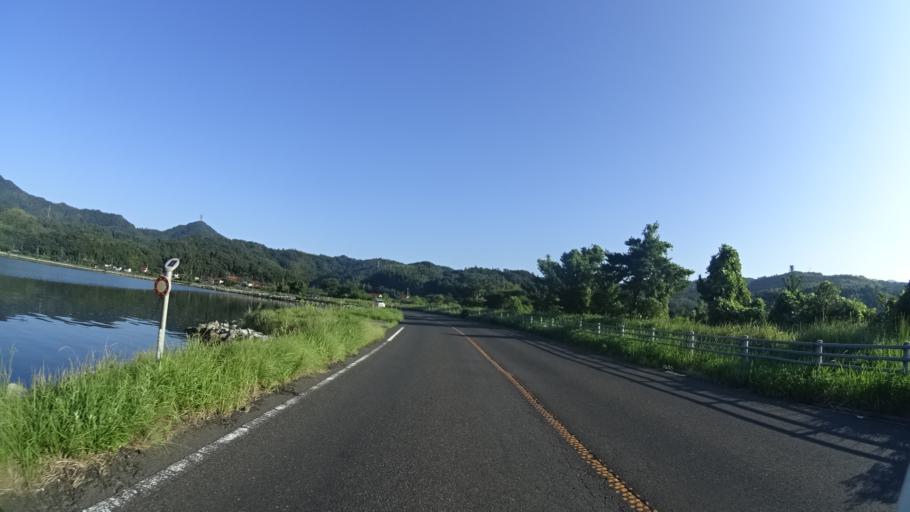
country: JP
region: Shimane
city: Sakaiminato
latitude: 35.5350
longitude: 133.1609
